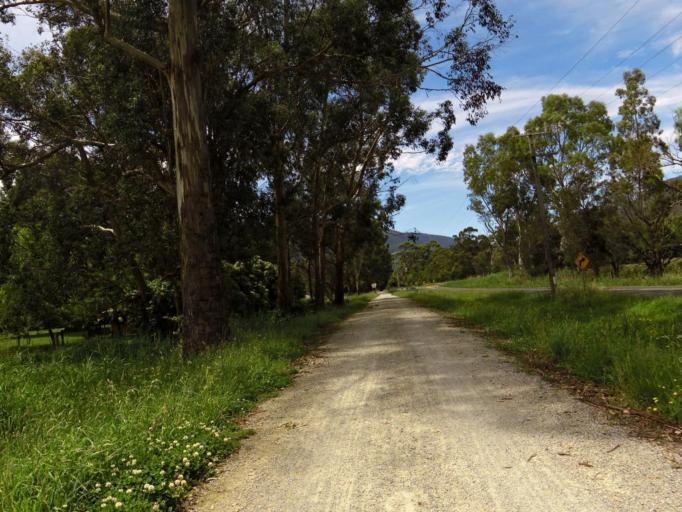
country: AU
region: Victoria
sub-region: Yarra Ranges
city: Millgrove
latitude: -37.7665
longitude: 145.6370
